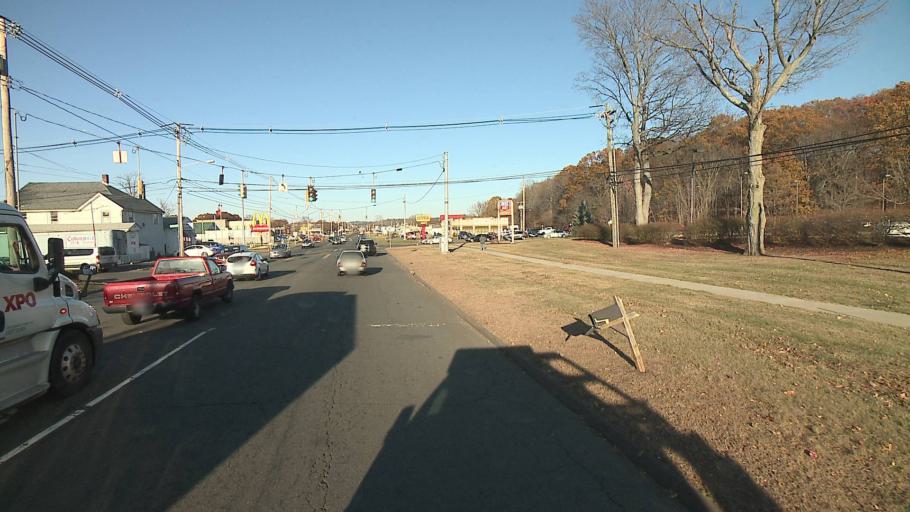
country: US
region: Connecticut
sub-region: New Haven County
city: Wallingford
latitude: 41.4694
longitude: -72.8168
